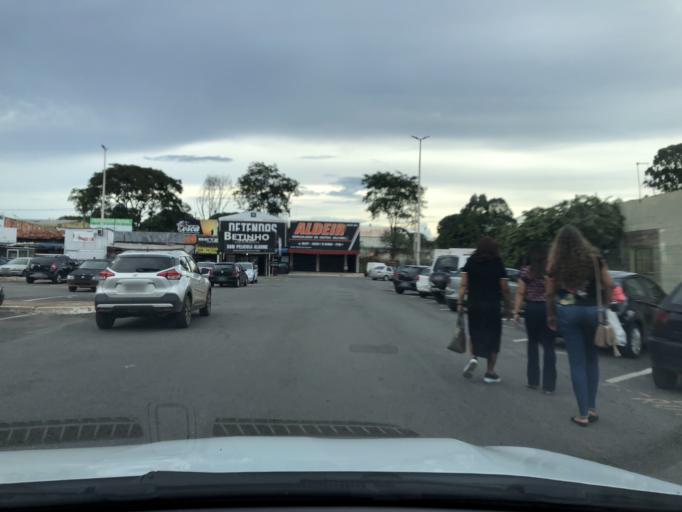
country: BR
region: Federal District
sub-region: Brasilia
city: Brasilia
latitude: -15.7950
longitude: -47.9508
